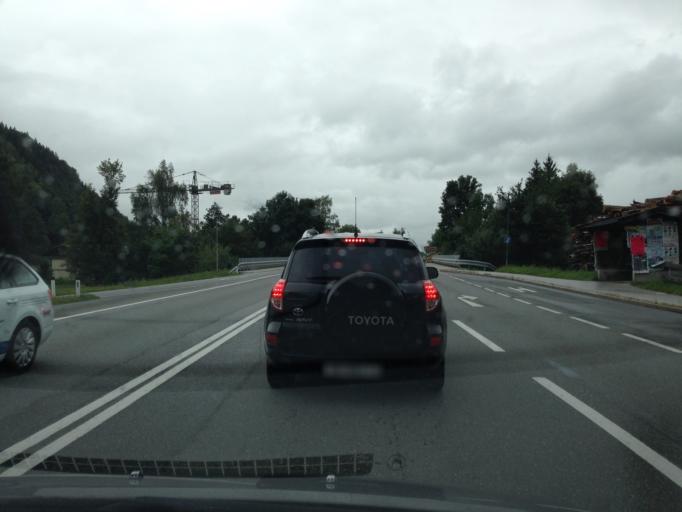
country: AT
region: Salzburg
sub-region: Politischer Bezirk Zell am See
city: Maishofen
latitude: 47.3597
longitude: 12.8000
